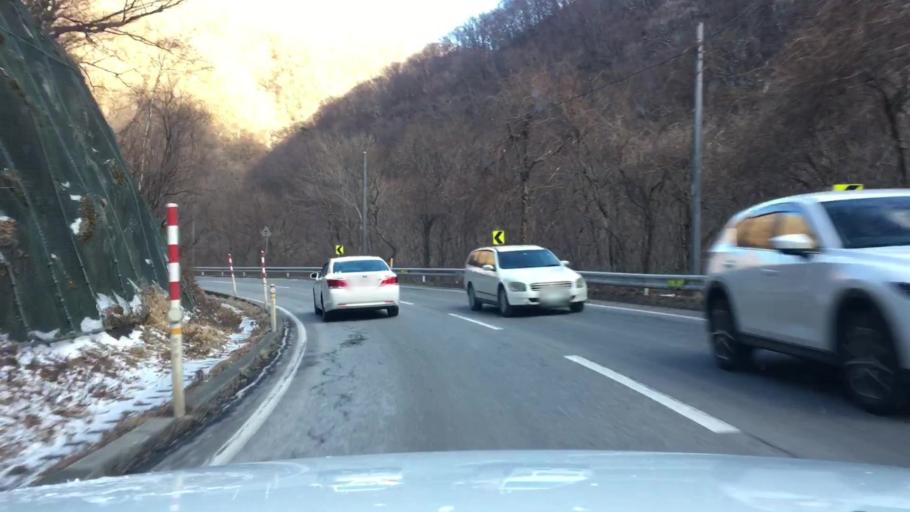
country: JP
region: Iwate
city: Tono
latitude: 39.6185
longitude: 141.5048
